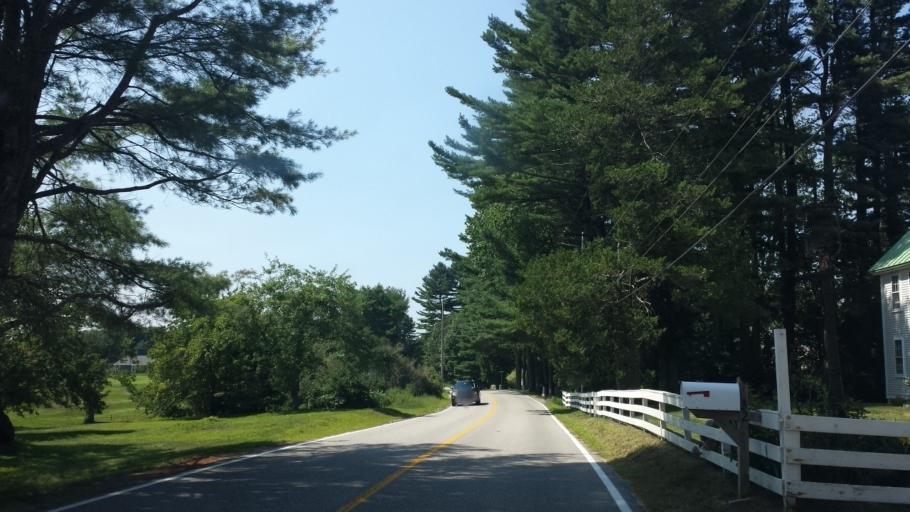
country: US
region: Maine
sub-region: York County
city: Arundel
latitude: 43.3747
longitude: -70.4790
